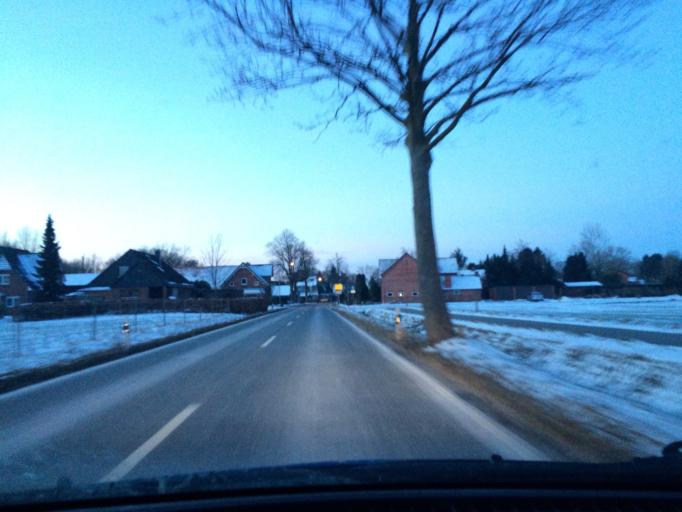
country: DE
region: Lower Saxony
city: Marschacht
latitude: 53.3928
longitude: 10.3506
